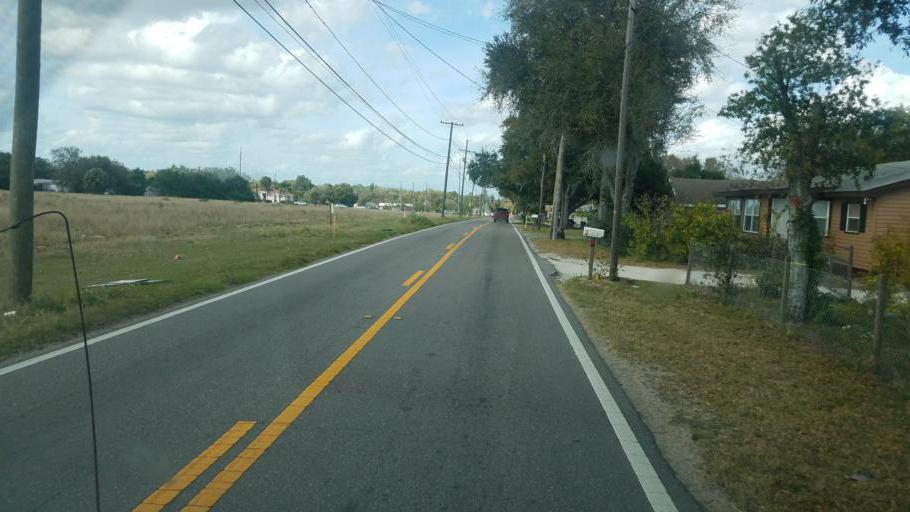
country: US
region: Florida
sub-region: Polk County
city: Haines City
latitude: 28.1042
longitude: -81.6068
